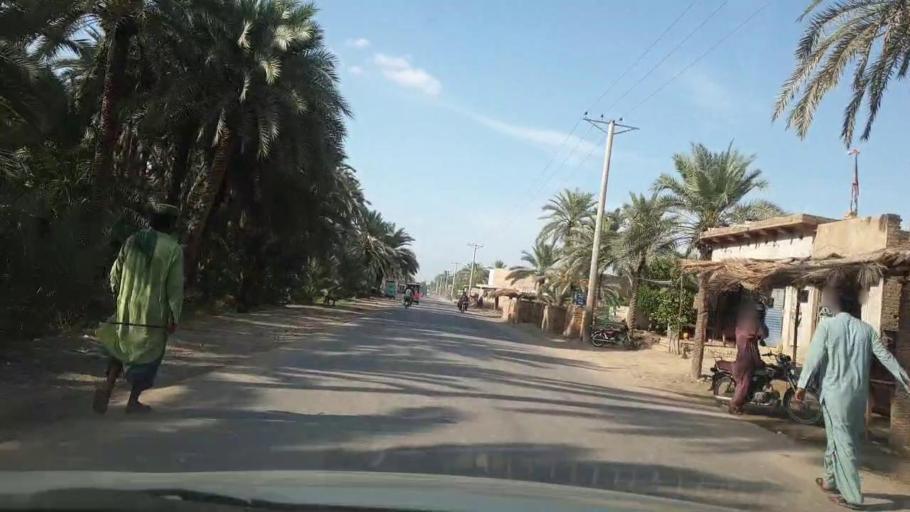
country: PK
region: Sindh
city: Sukkur
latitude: 27.6575
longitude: 68.8413
